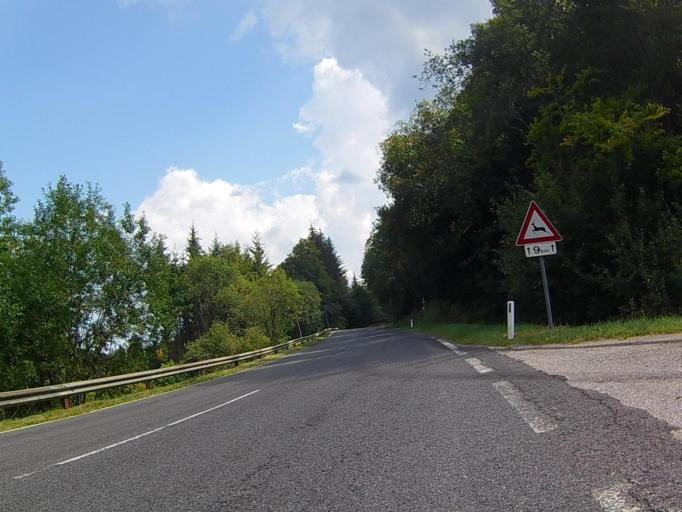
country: AT
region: Styria
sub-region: Politischer Bezirk Deutschlandsberg
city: Soboth
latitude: 46.7045
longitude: 15.0919
